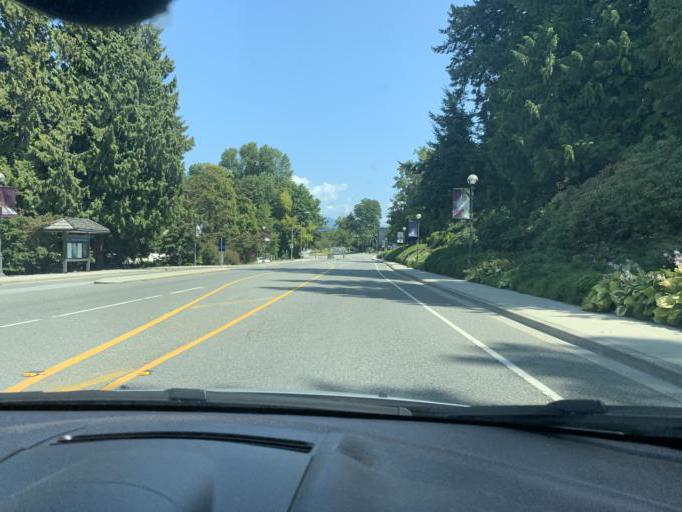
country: CA
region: British Columbia
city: West End
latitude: 49.2701
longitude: -123.2560
